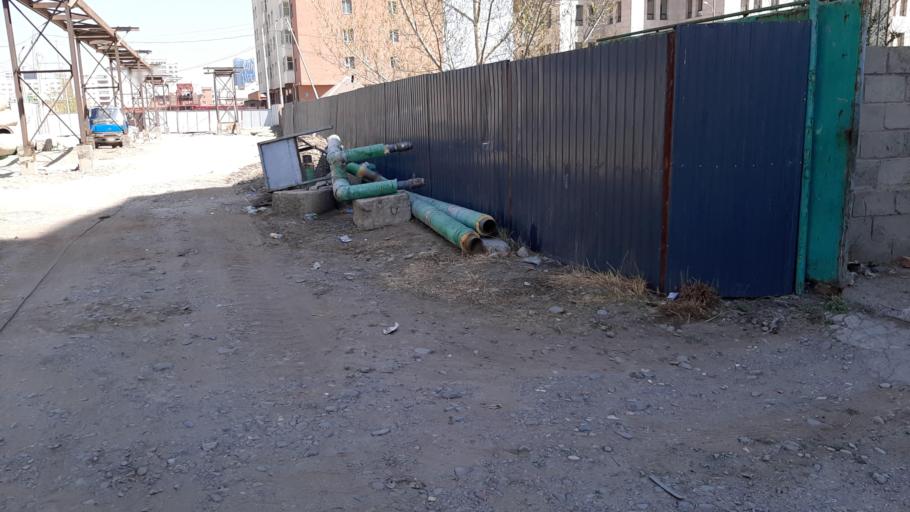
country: MN
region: Ulaanbaatar
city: Ulaanbaatar
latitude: 47.9061
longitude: 106.8929
